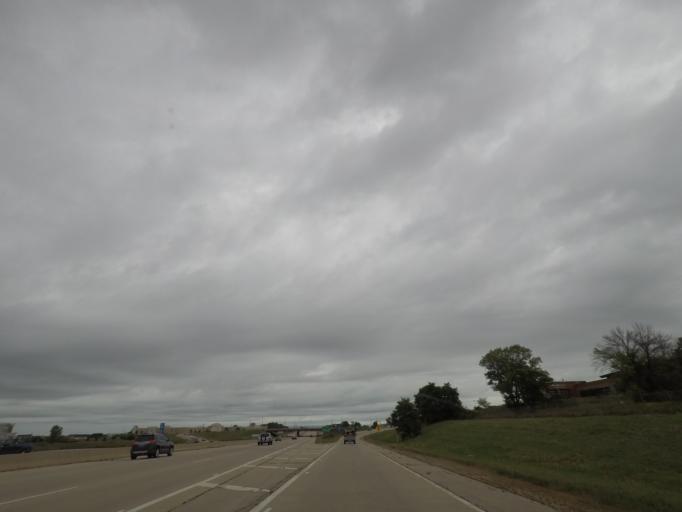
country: US
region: Wisconsin
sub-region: Dane County
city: Sun Prairie
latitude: 43.1584
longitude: -89.2702
